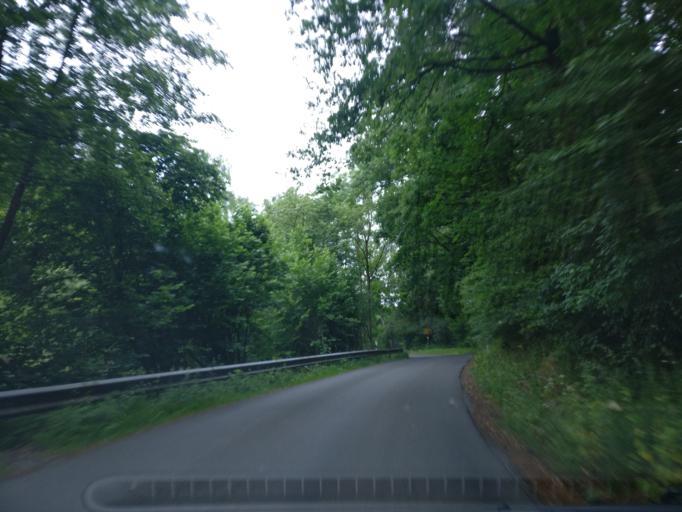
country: DE
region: Lower Saxony
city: Scheden
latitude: 51.4223
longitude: 9.7177
